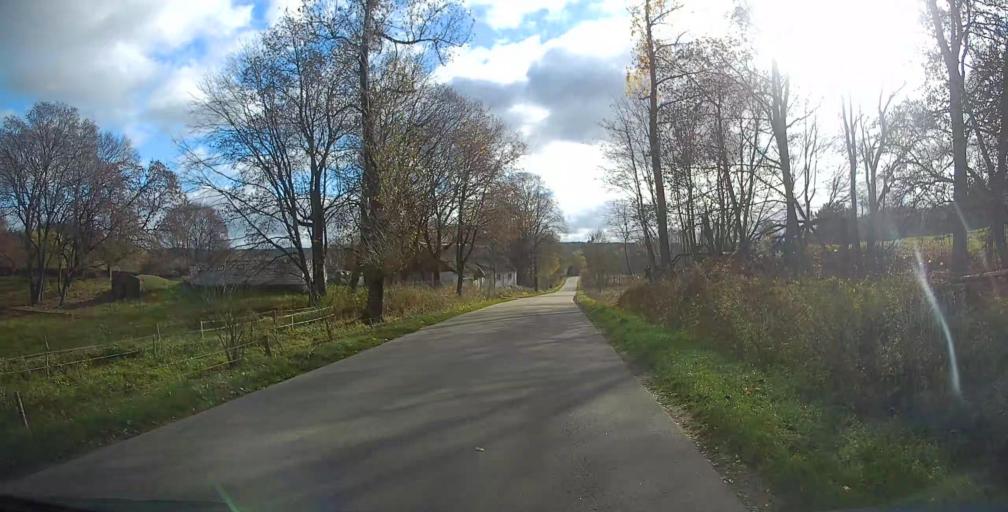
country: PL
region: Podlasie
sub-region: Suwalki
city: Suwalki
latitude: 54.2807
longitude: 22.9081
